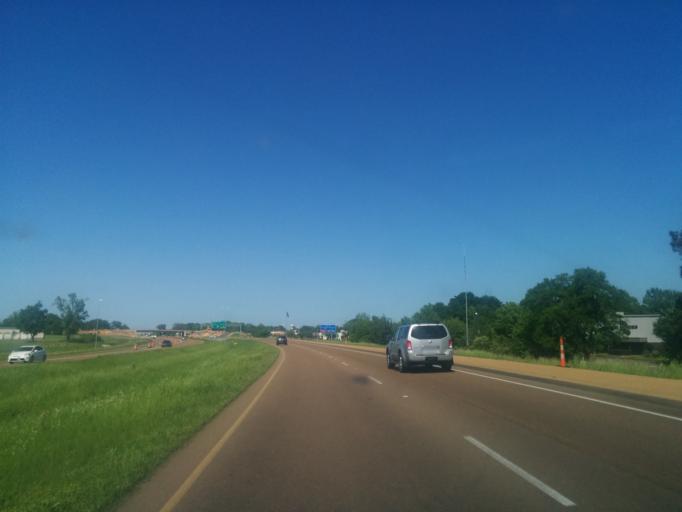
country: US
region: Mississippi
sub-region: Madison County
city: Madison
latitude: 32.5114
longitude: -90.1059
